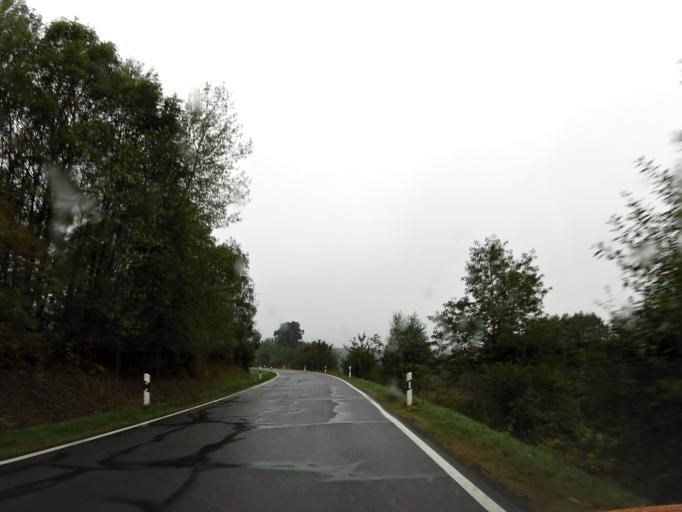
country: DE
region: Saxony-Anhalt
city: Hasselfelde
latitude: 51.6584
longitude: 10.8756
